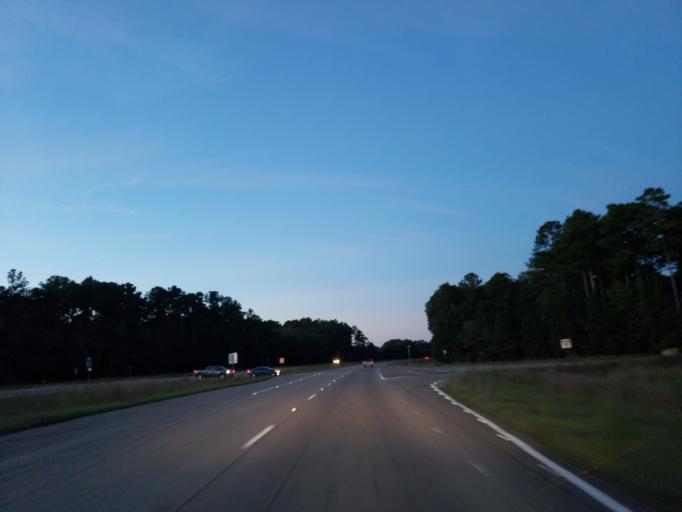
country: US
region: Mississippi
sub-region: Clarke County
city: Quitman
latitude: 31.8568
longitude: -88.7201
